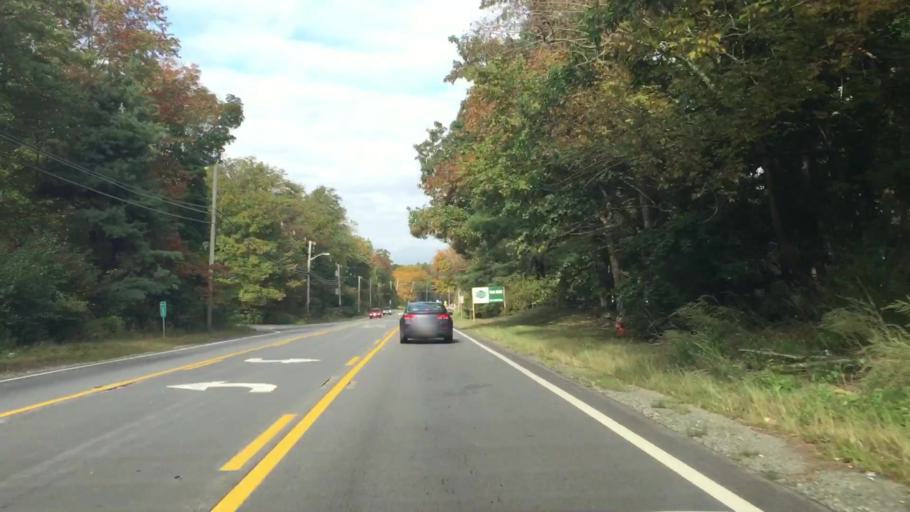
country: US
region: Massachusetts
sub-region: Middlesex County
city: North Reading
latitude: 42.6340
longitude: -71.0725
